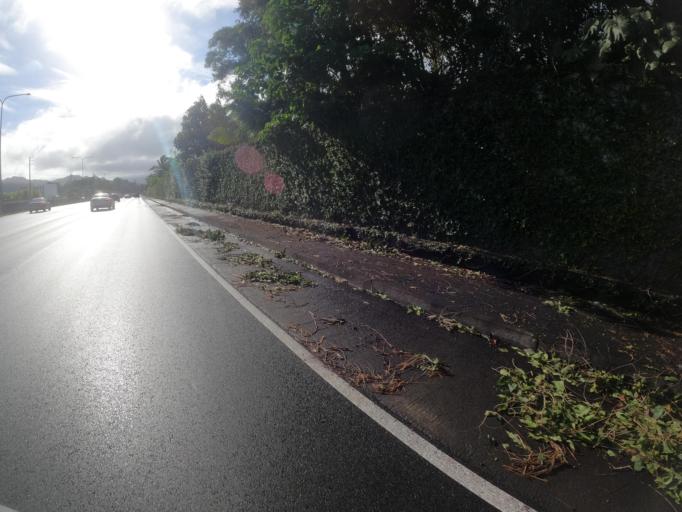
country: US
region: Hawaii
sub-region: Honolulu County
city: Kane'ohe
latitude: 21.4143
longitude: -157.8115
